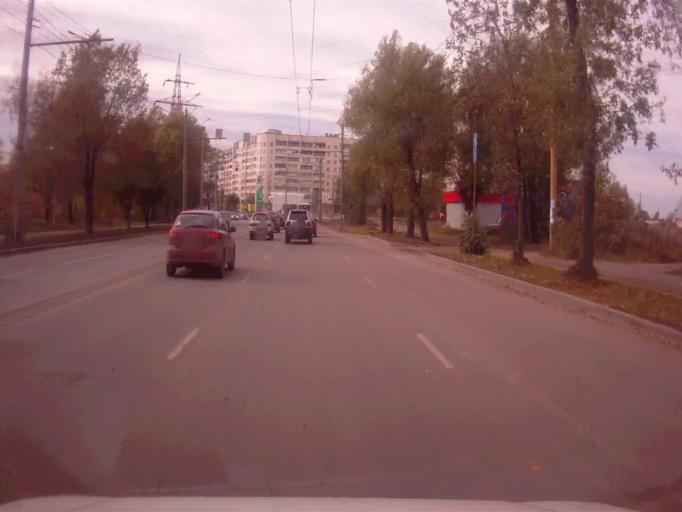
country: RU
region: Chelyabinsk
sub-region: Gorod Chelyabinsk
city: Chelyabinsk
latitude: 55.1163
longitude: 61.4449
